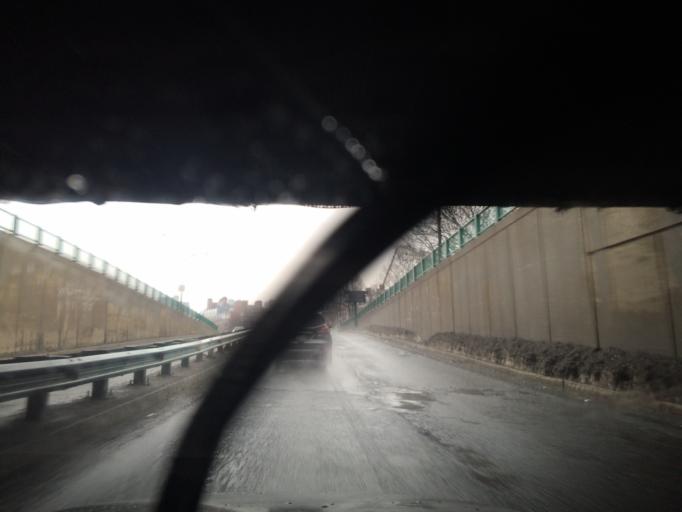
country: US
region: Massachusetts
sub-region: Middlesex County
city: Cambridge
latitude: 42.3685
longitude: -71.1241
